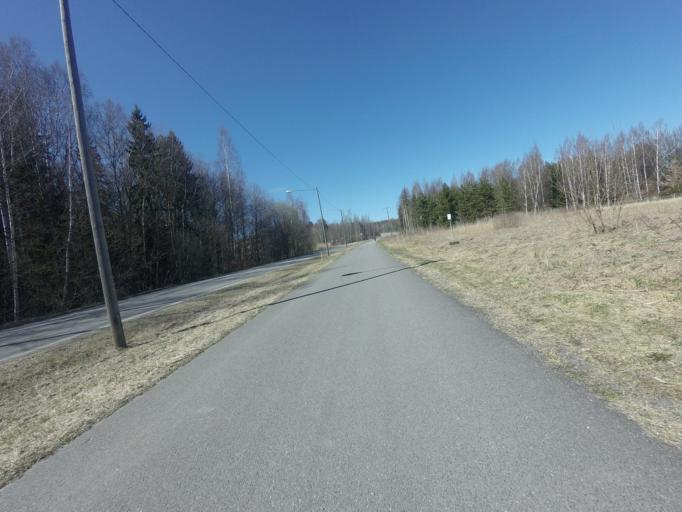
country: FI
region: Varsinais-Suomi
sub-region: Turku
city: Raisio
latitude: 60.4533
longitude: 22.1758
